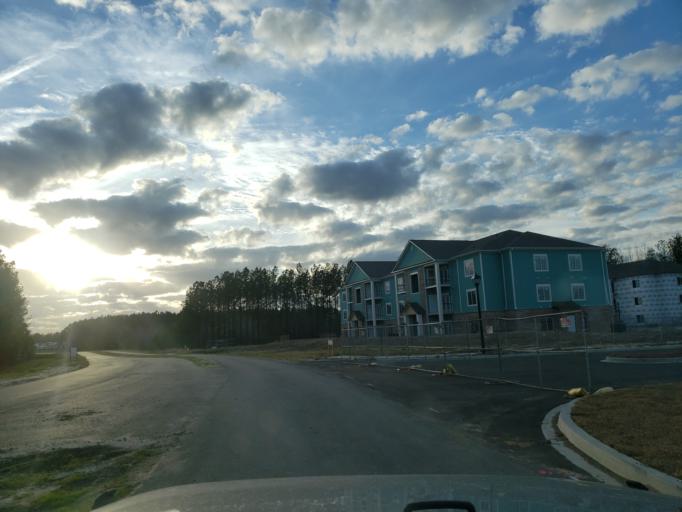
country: US
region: Georgia
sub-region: Chatham County
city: Port Wentworth
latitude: 32.2221
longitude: -81.1889
